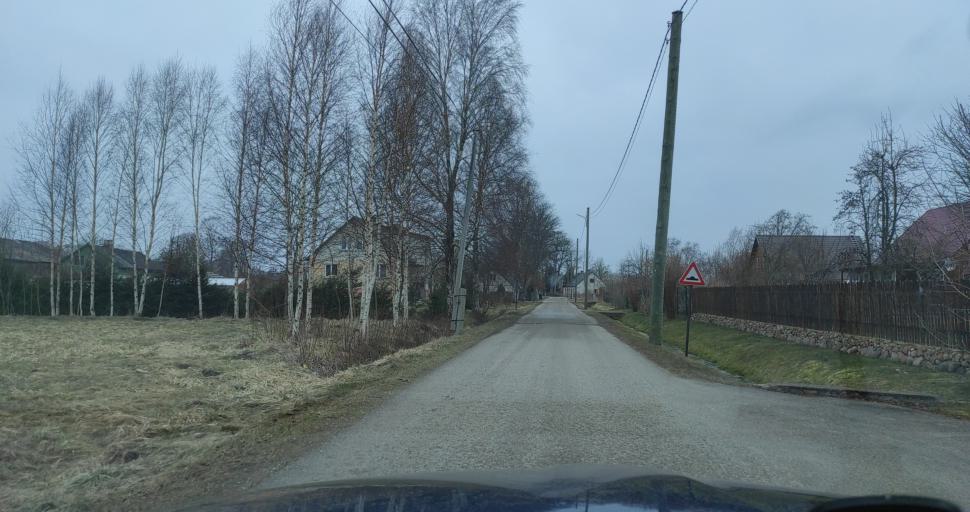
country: LV
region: Ventspils Rajons
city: Piltene
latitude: 57.2234
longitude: 21.6859
